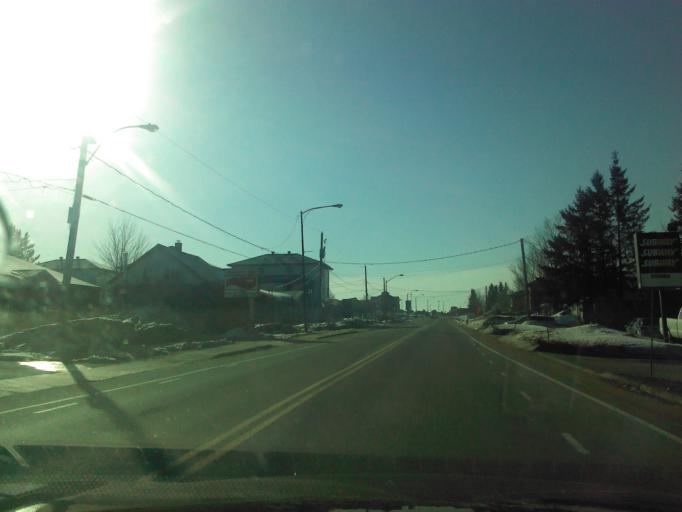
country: CA
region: Quebec
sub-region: Capitale-Nationale
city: Sainte Catherine de la Jacques Cartier
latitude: 46.8435
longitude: -71.6139
